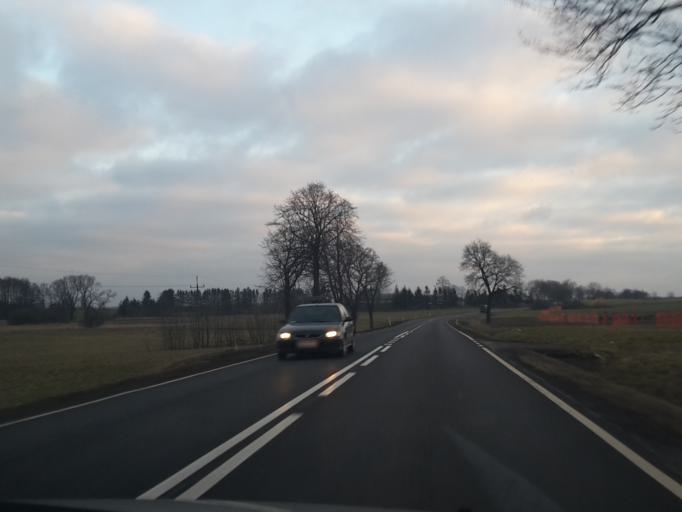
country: PL
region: Warmian-Masurian Voivodeship
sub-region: Powiat ilawski
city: Lubawa
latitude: 53.5679
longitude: 19.7831
